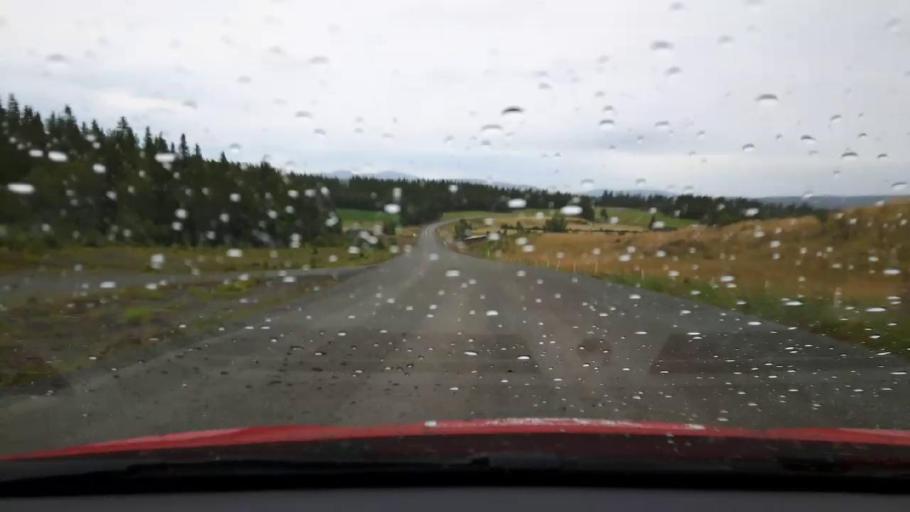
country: SE
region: Jaemtland
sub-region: Are Kommun
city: Are
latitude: 63.4731
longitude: 12.5645
